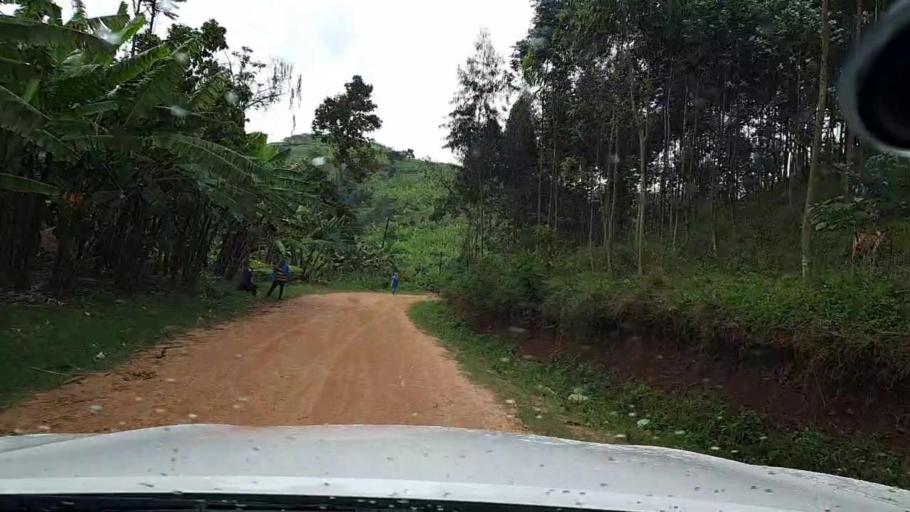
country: RW
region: Western Province
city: Kibuye
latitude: -2.1138
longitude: 29.4201
